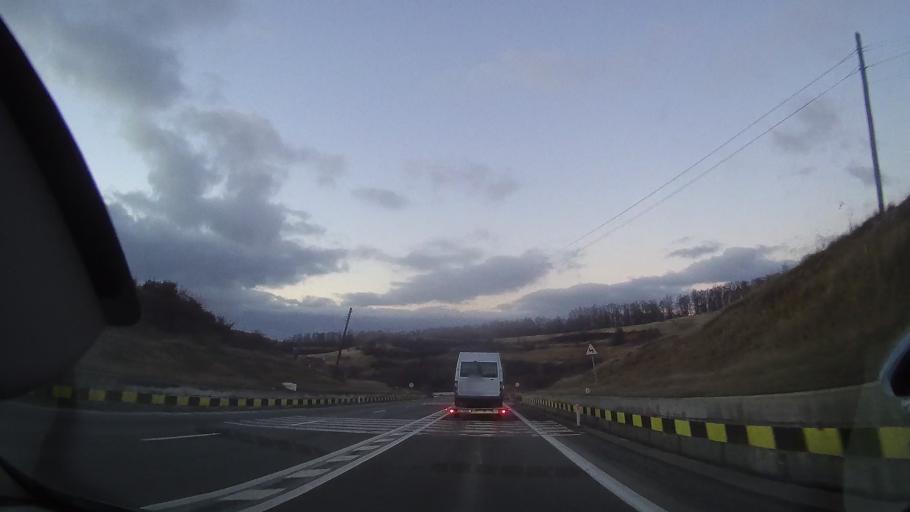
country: RO
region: Cluj
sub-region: Comuna Izvoru Crisului
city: Izvoru Crisului
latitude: 46.8278
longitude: 23.1531
